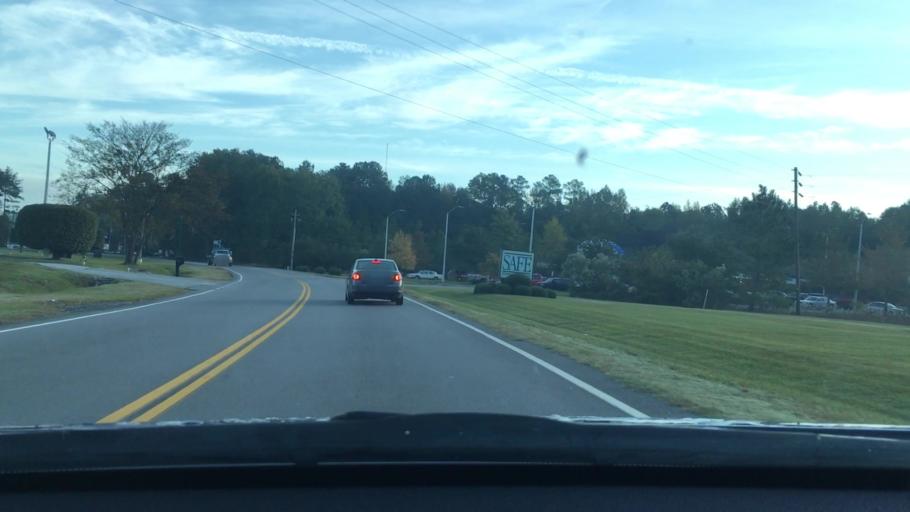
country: US
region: South Carolina
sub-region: Sumter County
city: Sumter
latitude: 33.9254
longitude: -80.3281
